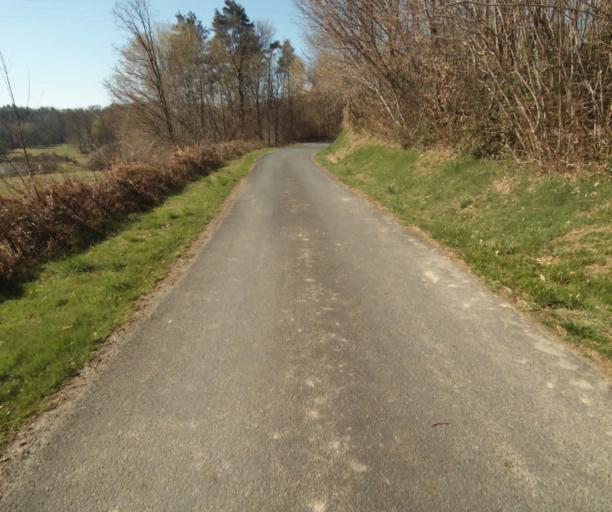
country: FR
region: Limousin
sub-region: Departement de la Correze
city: Saint-Mexant
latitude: 45.3119
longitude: 1.6208
